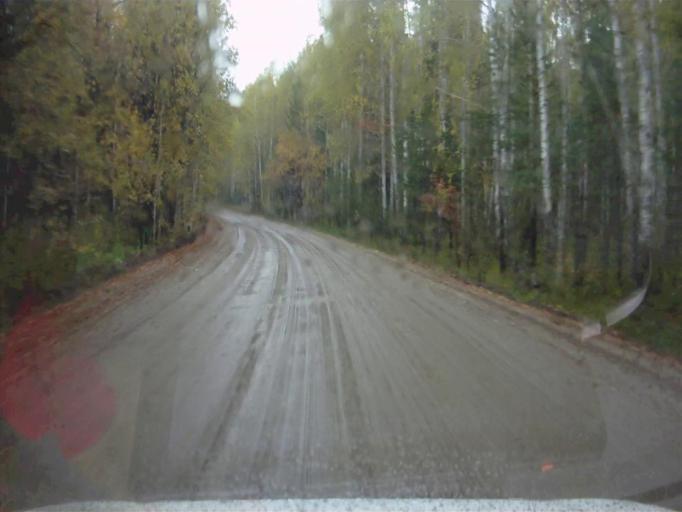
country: RU
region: Chelyabinsk
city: Kyshtym
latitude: 55.8854
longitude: 60.4652
